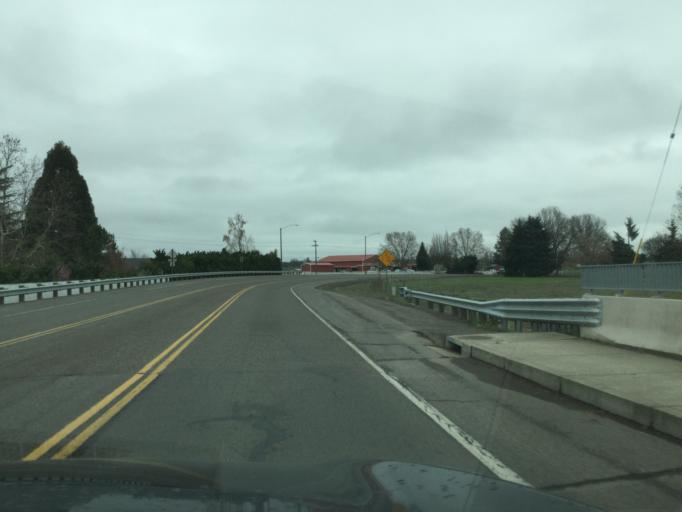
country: US
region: Oregon
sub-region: Jackson County
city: Central Point
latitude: 42.3913
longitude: -122.9183
